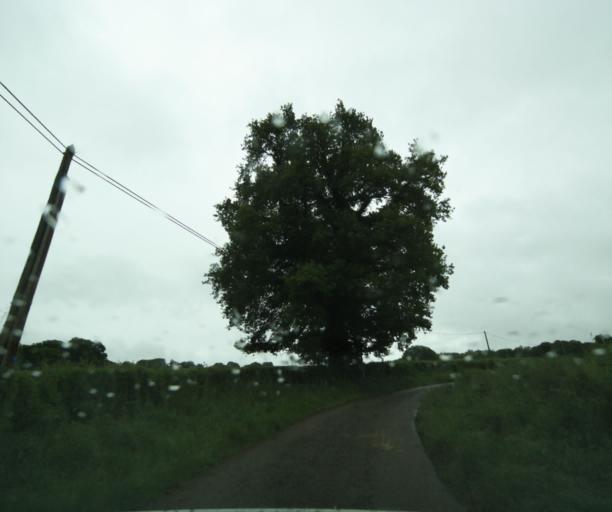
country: FR
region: Bourgogne
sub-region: Departement de Saone-et-Loire
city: Charolles
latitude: 46.4855
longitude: 4.2920
